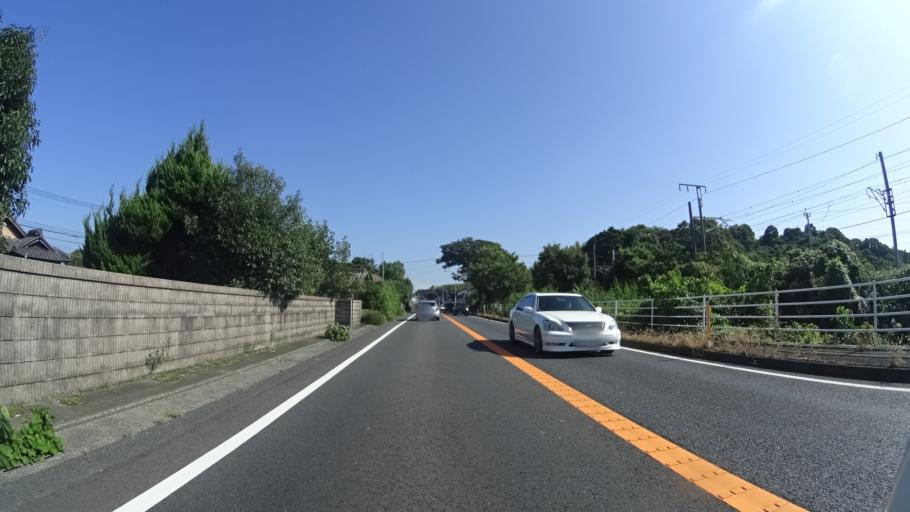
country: JP
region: Fukuoka
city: Shiida
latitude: 33.6405
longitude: 131.0698
